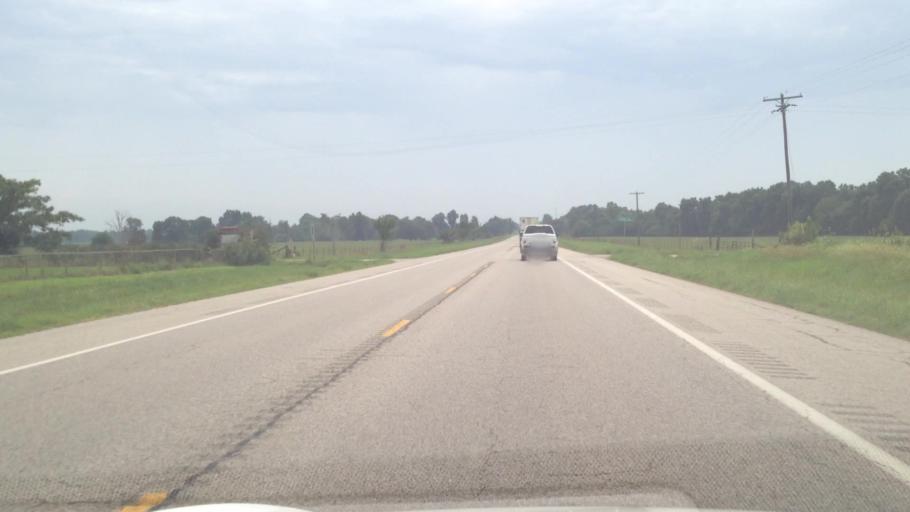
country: US
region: Missouri
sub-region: Jasper County
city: Carl Junction
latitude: 37.2080
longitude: -94.7048
